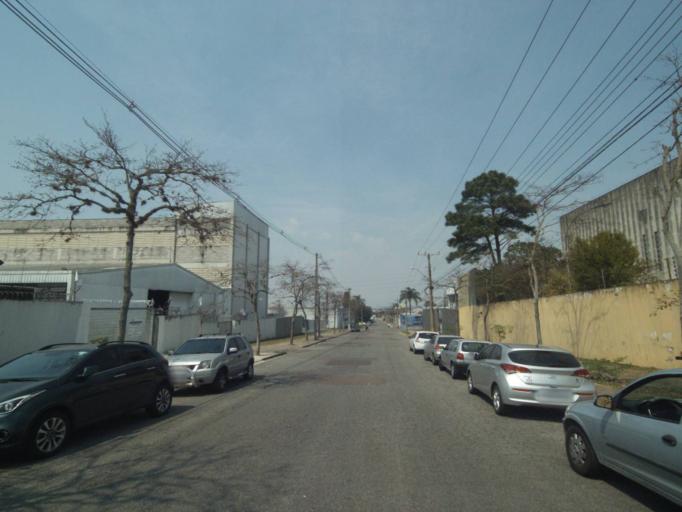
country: BR
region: Parana
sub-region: Curitiba
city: Curitiba
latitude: -25.4619
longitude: -49.2580
